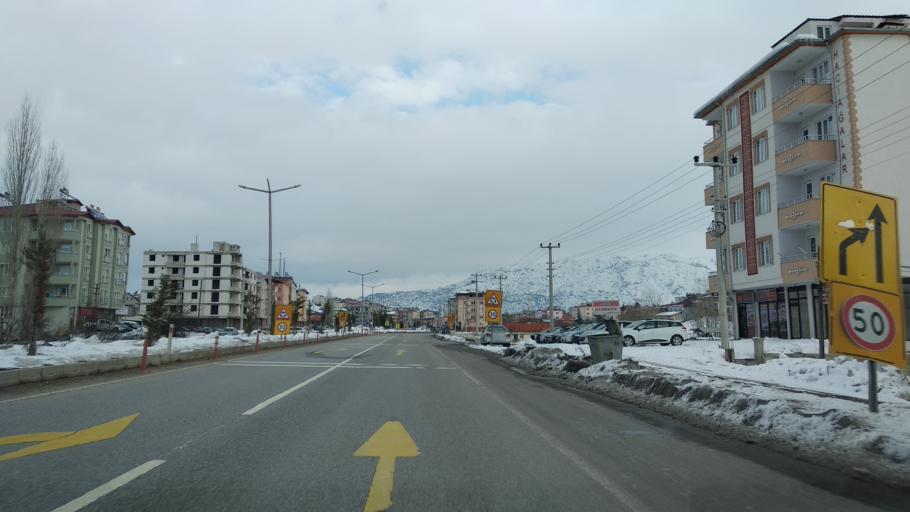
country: TR
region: Kahramanmaras
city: Goksun
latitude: 38.0261
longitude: 36.4932
